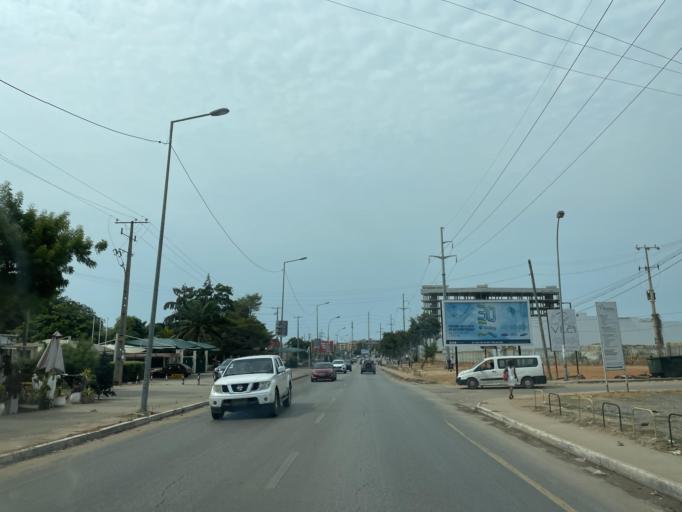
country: AO
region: Luanda
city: Luanda
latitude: -8.9061
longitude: 13.1996
